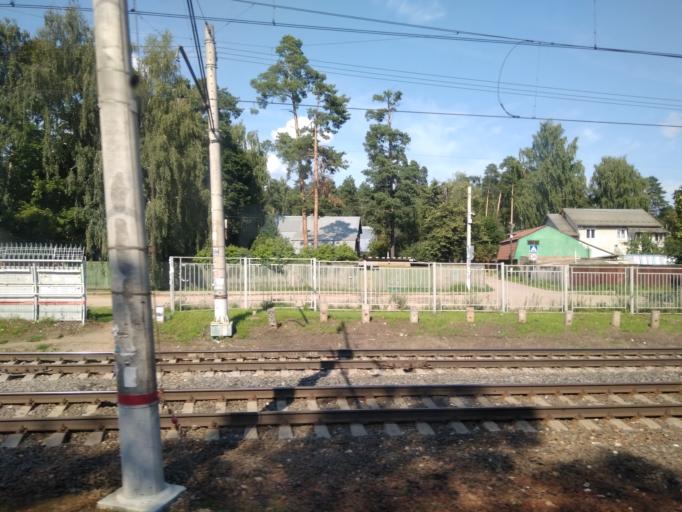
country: RU
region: Moskovskaya
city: Il'inskiy
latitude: 55.6146
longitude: 38.1046
